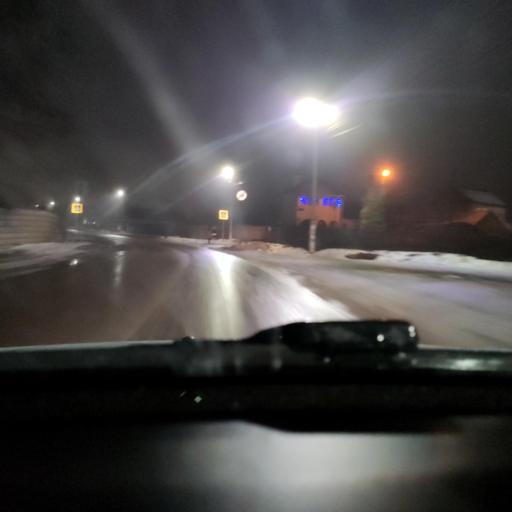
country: RU
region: Voronezj
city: Podgornoye
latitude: 51.7923
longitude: 39.1469
